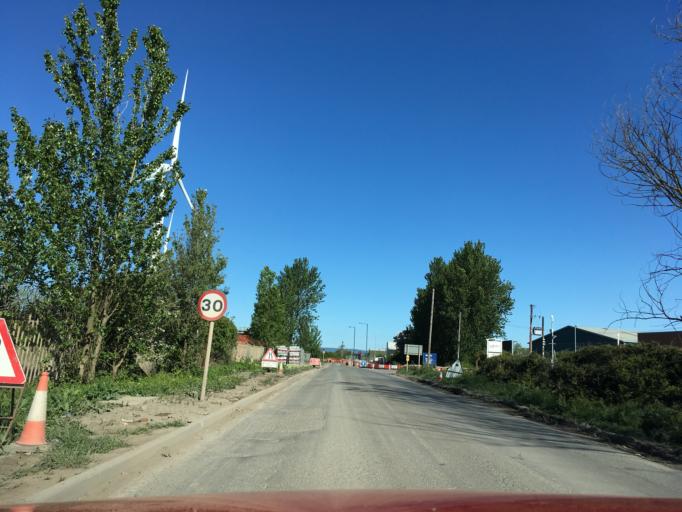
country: GB
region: England
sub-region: South Gloucestershire
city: Severn Beach
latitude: 51.5323
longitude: -2.6699
